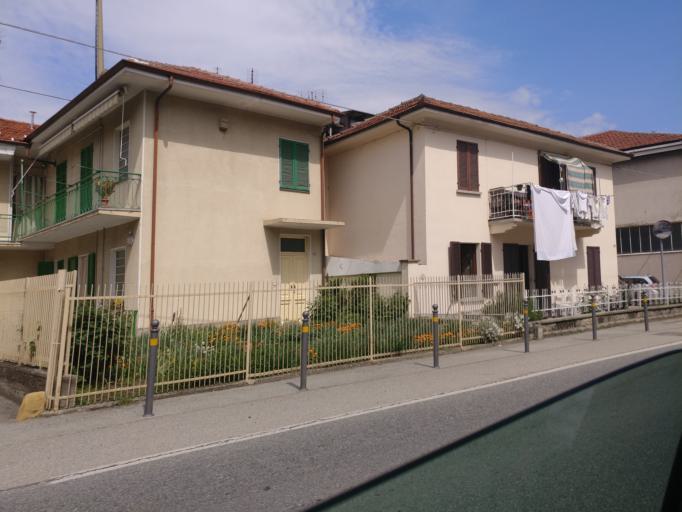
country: IT
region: Piedmont
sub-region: Provincia di Torino
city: Cavour
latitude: 44.7840
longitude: 7.3787
